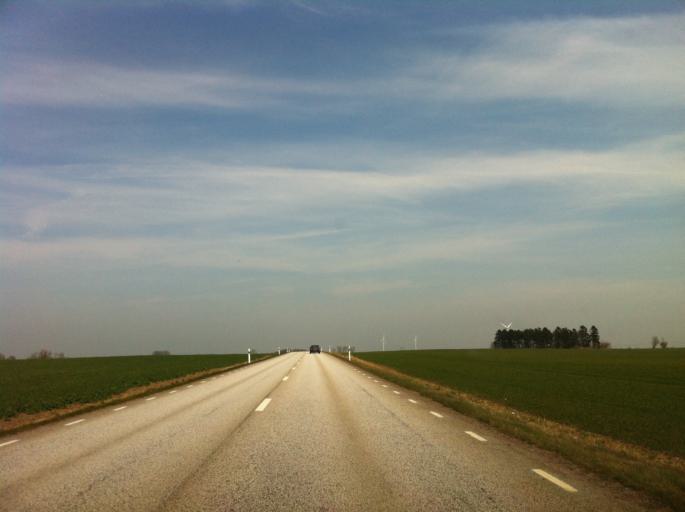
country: SE
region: Skane
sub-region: Svalovs Kommun
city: Teckomatorp
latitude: 55.8934
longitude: 13.0232
